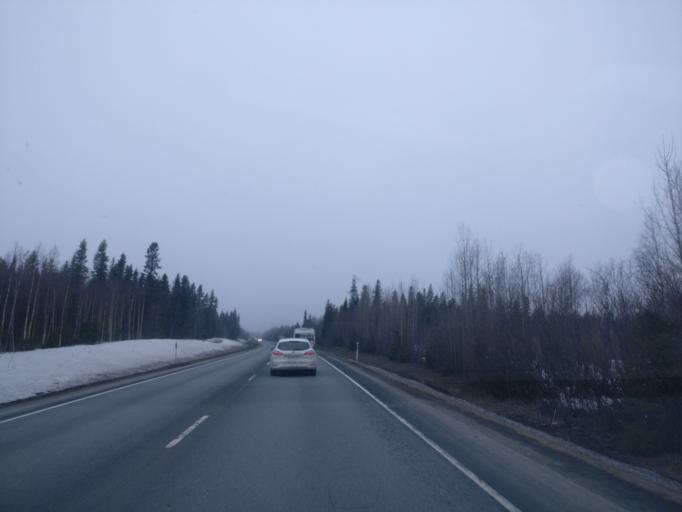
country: FI
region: Lapland
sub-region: Kemi-Tornio
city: Simo
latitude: 65.6748
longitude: 24.8895
